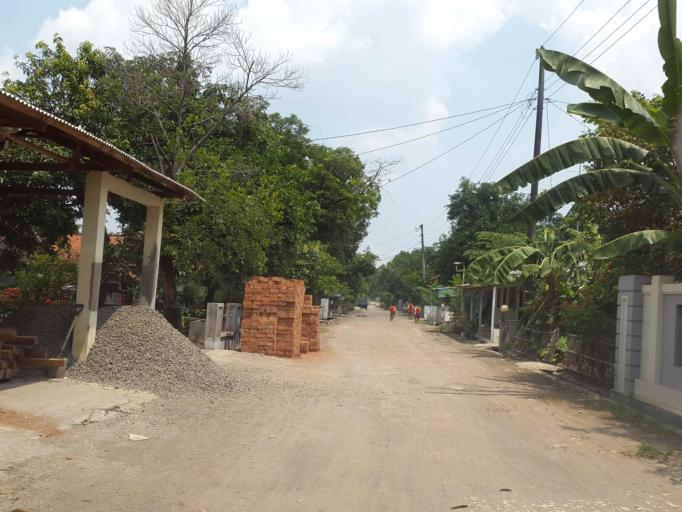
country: ID
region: West Java
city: Bantarpanjang
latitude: -6.9539
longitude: 108.7987
